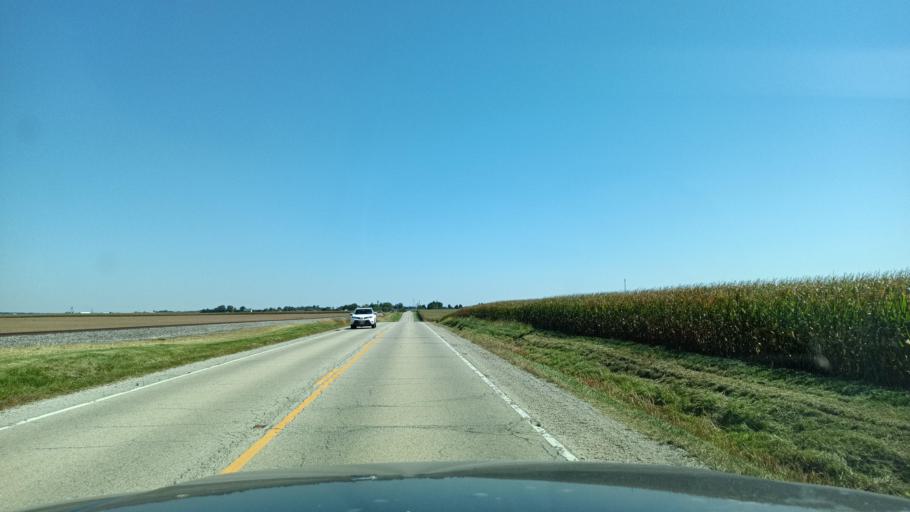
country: US
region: Illinois
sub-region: Tazewell County
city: Mackinaw
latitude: 40.6270
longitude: -89.3158
